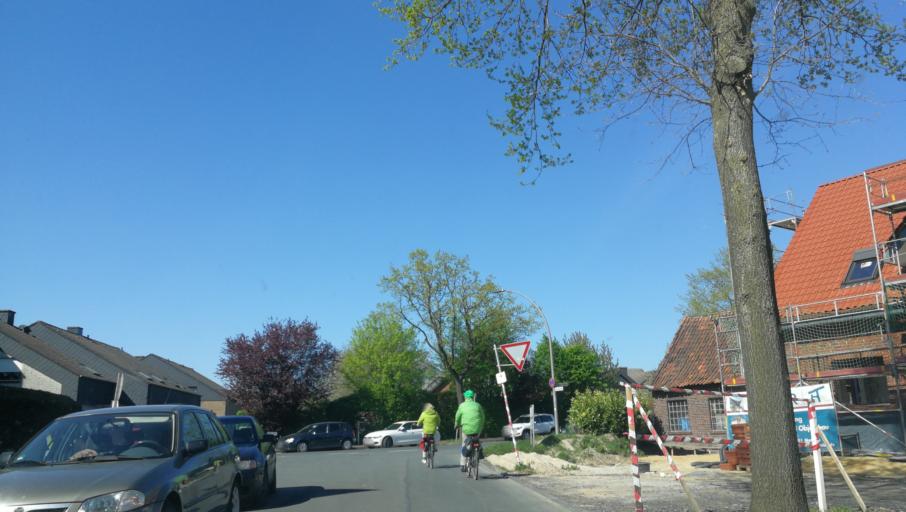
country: DE
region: North Rhine-Westphalia
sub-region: Regierungsbezirk Munster
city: Muenster
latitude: 51.9472
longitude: 7.5378
